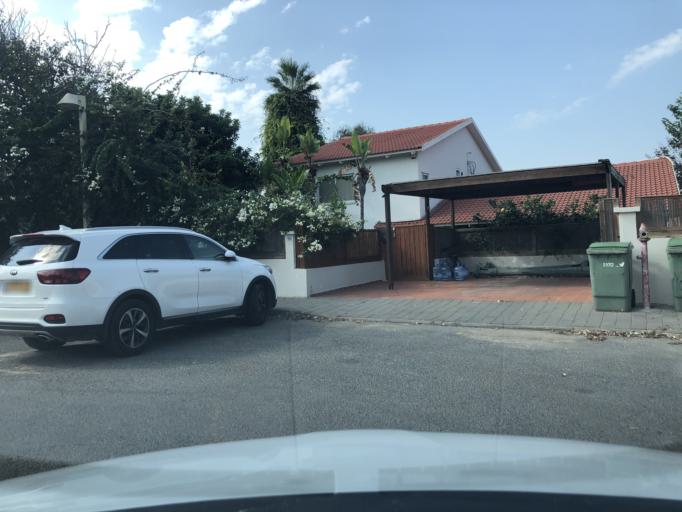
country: IL
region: Tel Aviv
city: Kefar Shemaryahu
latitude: 32.2161
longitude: 34.8163
